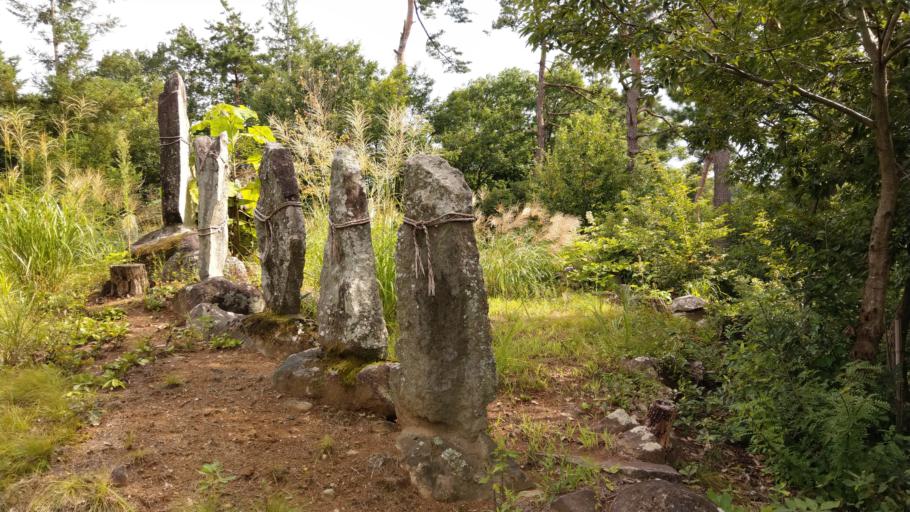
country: JP
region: Nagano
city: Saku
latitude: 36.2576
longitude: 138.5096
